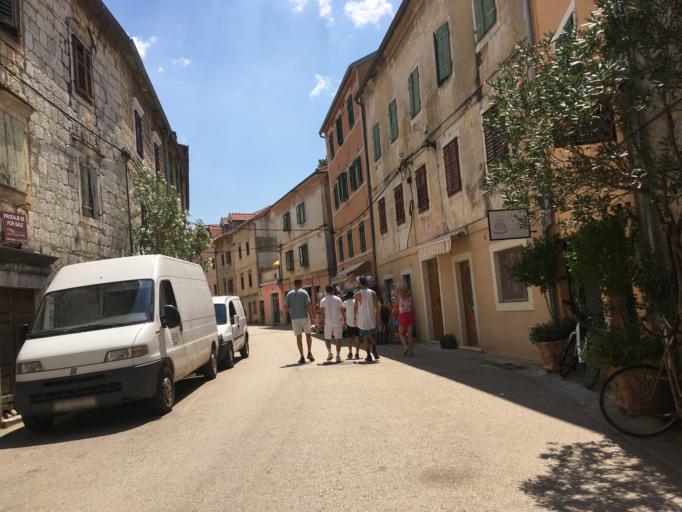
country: HR
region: Sibensko-Kniniska
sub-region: Grad Sibenik
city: Sibenik
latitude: 43.8201
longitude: 15.9222
